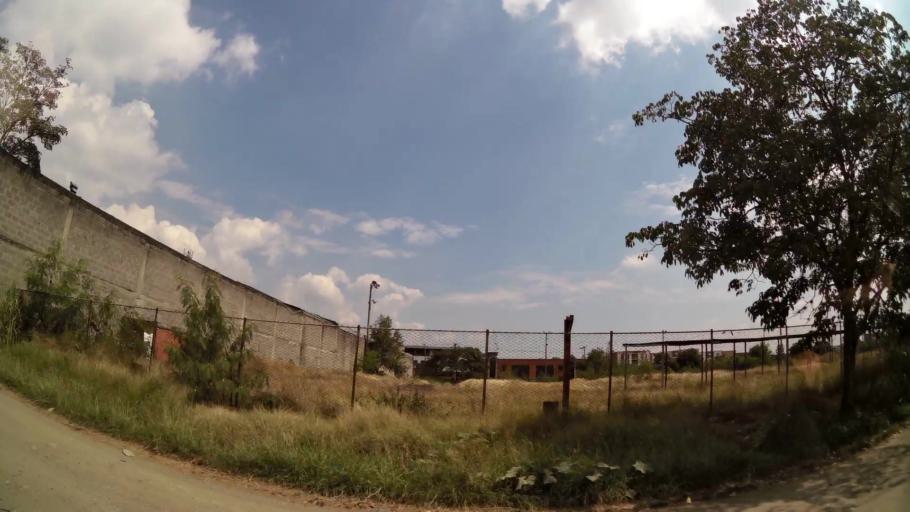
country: CO
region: Valle del Cauca
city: Cali
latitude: 3.4912
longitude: -76.5077
